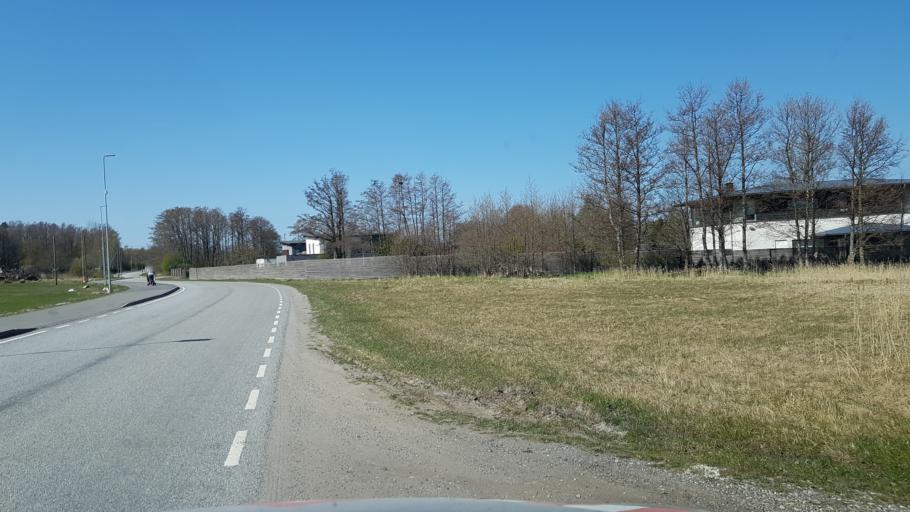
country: EE
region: Harju
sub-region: Viimsi vald
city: Viimsi
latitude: 59.5479
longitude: 24.8754
